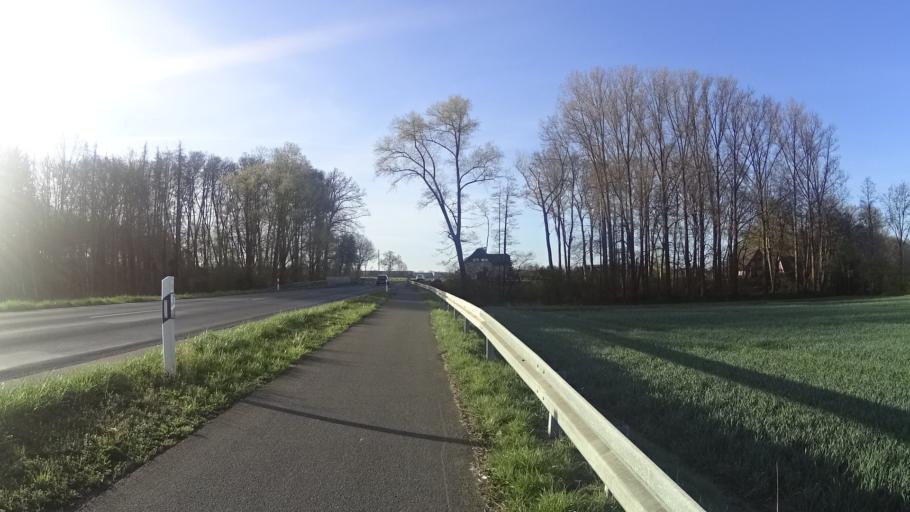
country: DE
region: North Rhine-Westphalia
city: Emsdetten
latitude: 52.1492
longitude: 7.5337
